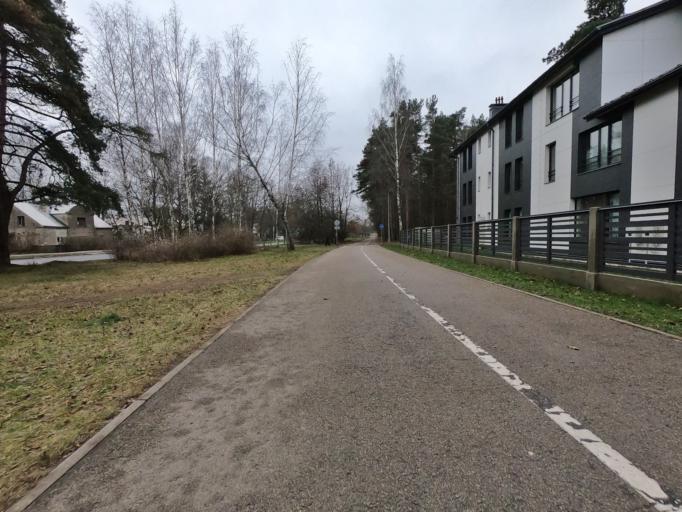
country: LV
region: Marupe
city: Marupe
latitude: 56.9567
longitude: 24.0234
